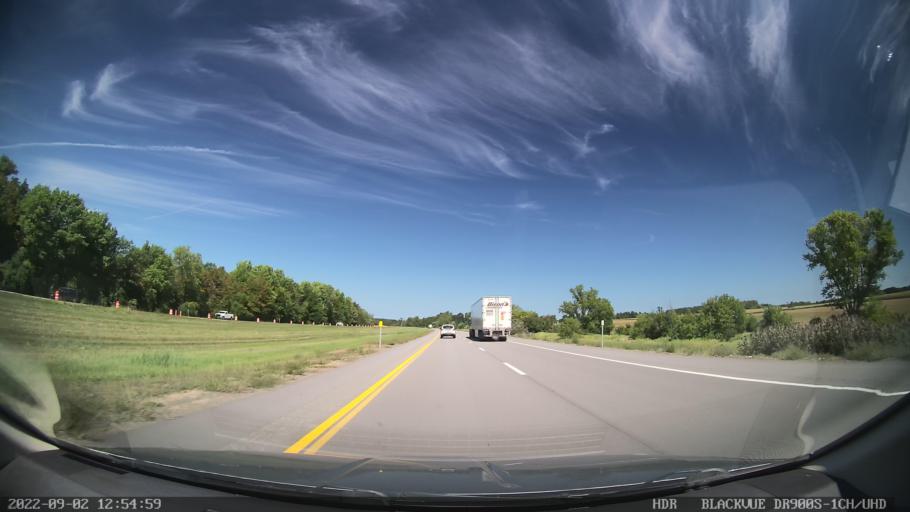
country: US
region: New York
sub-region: Livingston County
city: Avon
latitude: 42.9329
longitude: -77.6911
